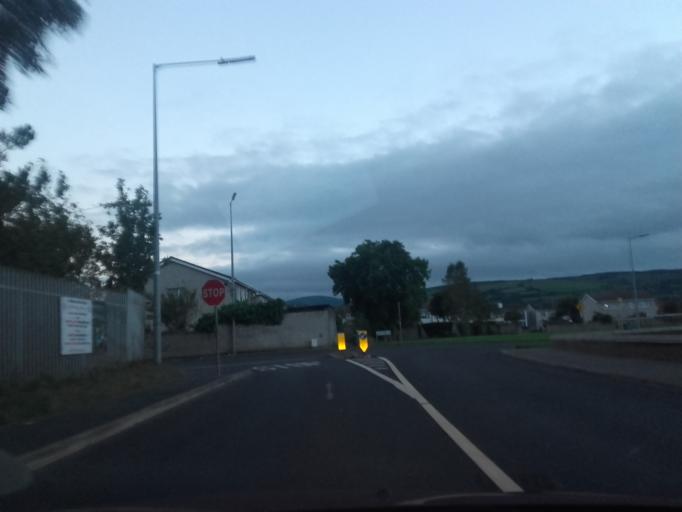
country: IE
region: Leinster
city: Tallaght
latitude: 53.2865
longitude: -6.3895
